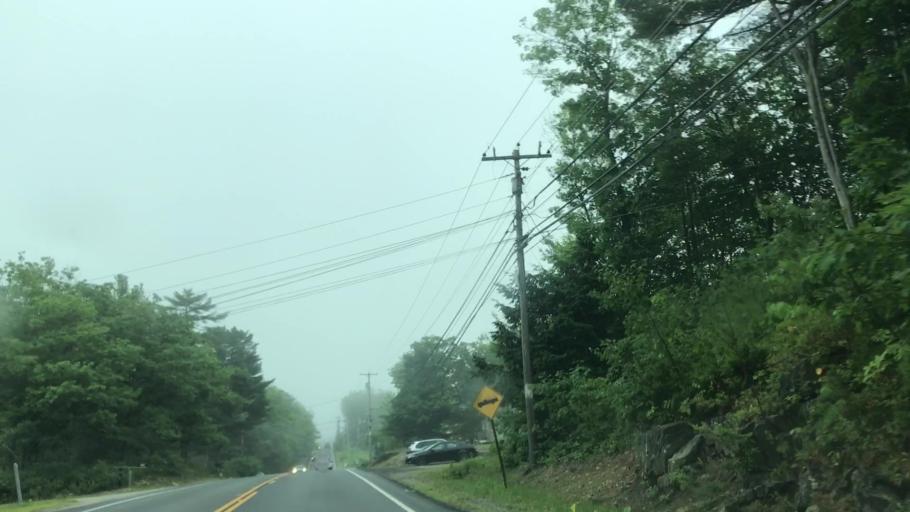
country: US
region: Maine
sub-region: Sagadahoc County
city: Bath
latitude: 43.9038
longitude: -69.8523
